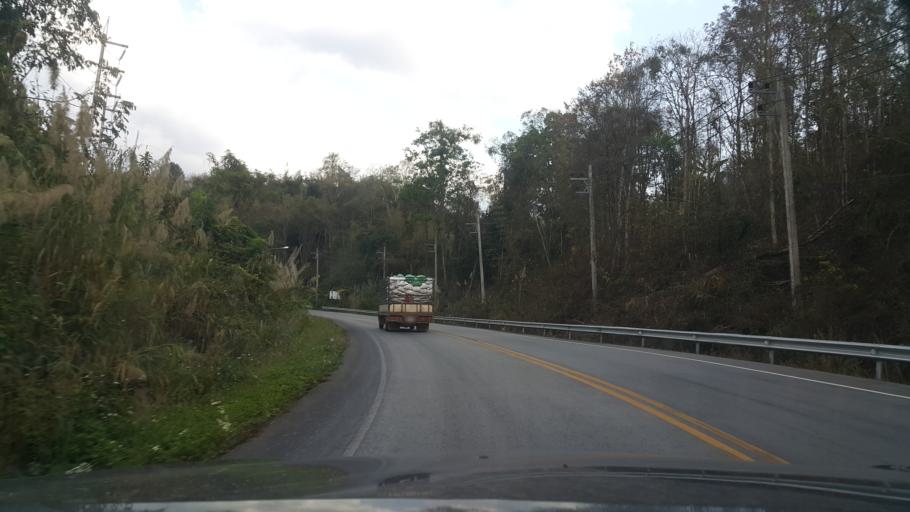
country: TH
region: Loei
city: Dan Sai
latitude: 17.2518
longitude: 101.1162
